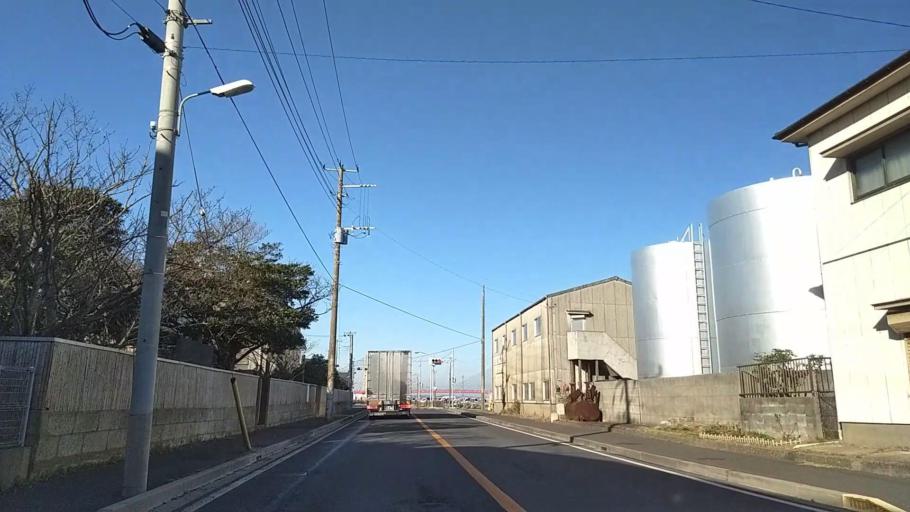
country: JP
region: Chiba
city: Hasaki
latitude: 35.7349
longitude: 140.8332
